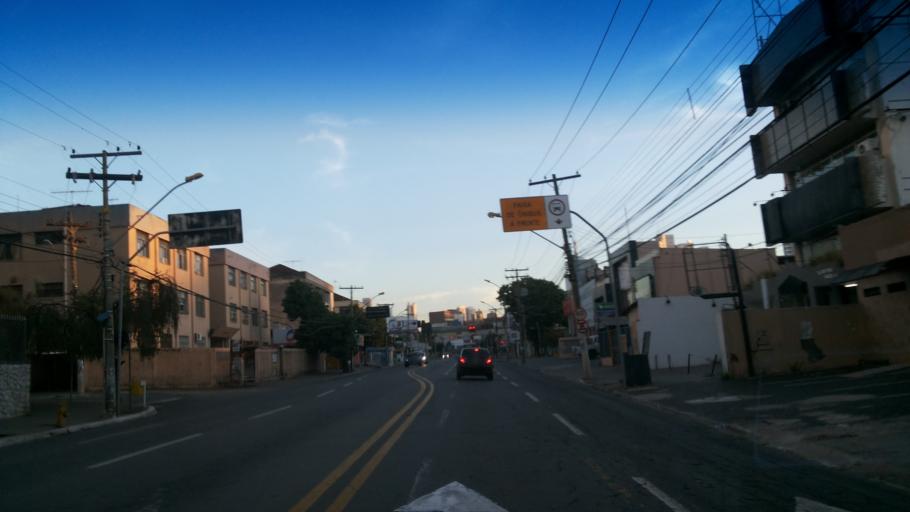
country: BR
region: Goias
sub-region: Goiania
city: Goiania
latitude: -16.6834
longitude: -49.2579
